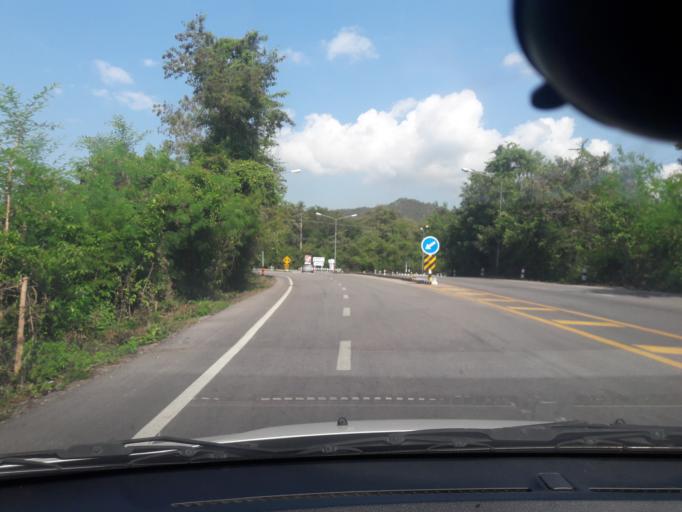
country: TH
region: Lampang
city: Mae Tha
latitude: 18.1870
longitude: 99.5479
